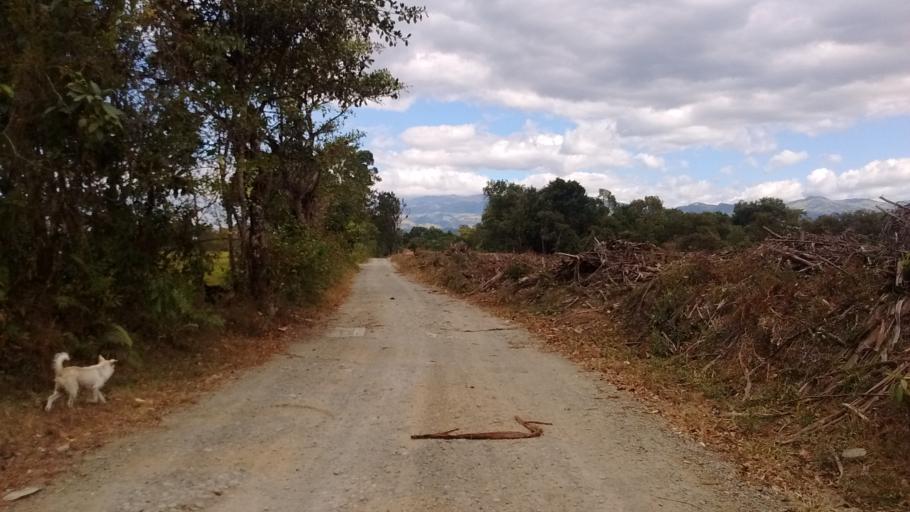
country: CO
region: Cauca
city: Popayan
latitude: 2.4956
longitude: -76.5910
